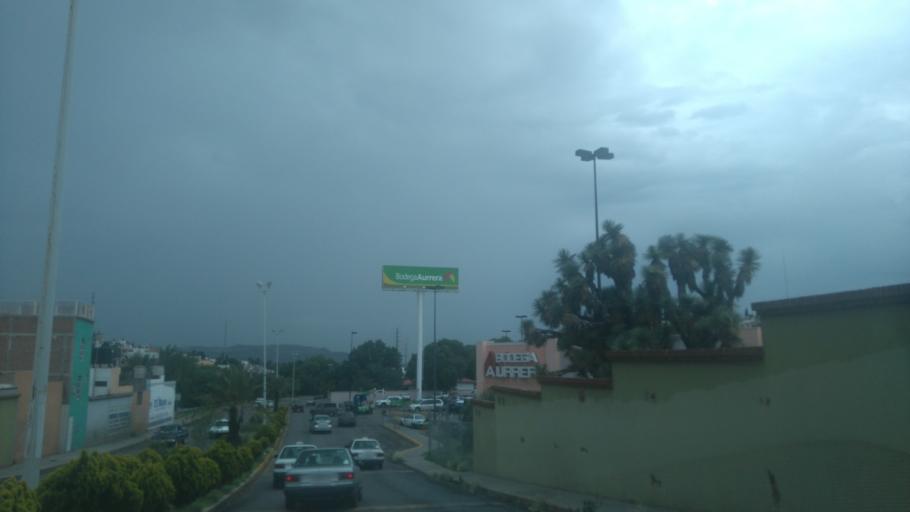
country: MX
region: Zacatecas
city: Zacatecas
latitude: 22.7602
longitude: -102.5839
